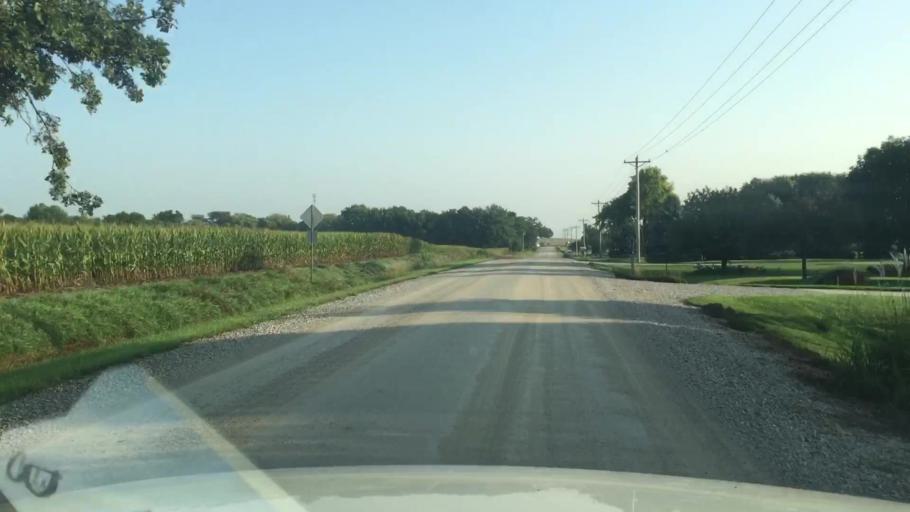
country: US
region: Iowa
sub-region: Story County
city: Huxley
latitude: 41.9127
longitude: -93.5766
